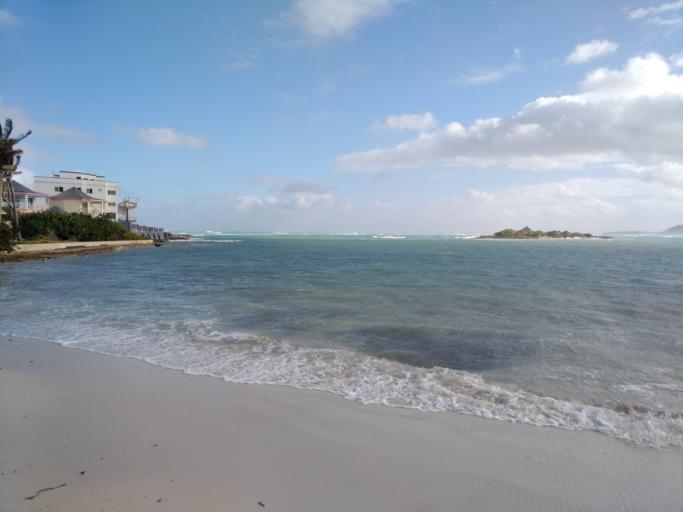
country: AI
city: Island Harbour
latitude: 18.2589
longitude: -63.0049
